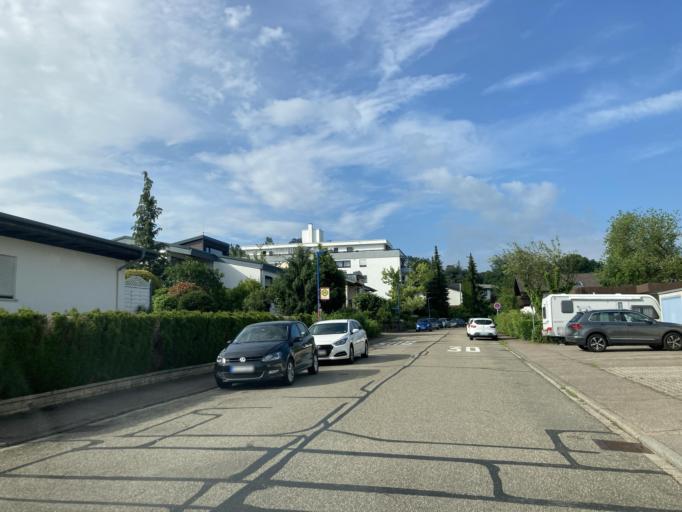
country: DE
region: Baden-Wuerttemberg
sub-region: Karlsruhe Region
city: Ettlingen
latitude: 48.9098
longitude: 8.4694
